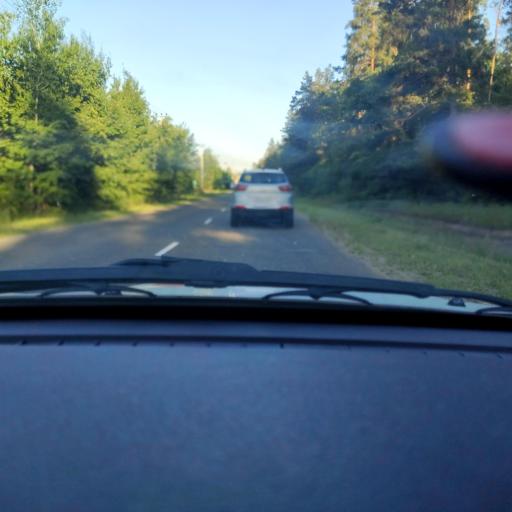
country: RU
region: Voronezj
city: Ramon'
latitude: 51.8896
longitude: 39.2480
